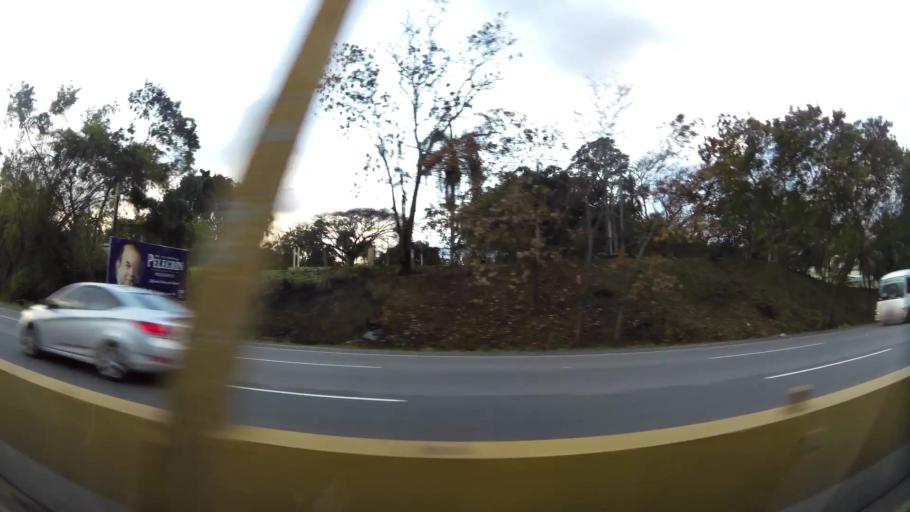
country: DO
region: Santo Domingo
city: Santo Domingo Oeste
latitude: 18.5606
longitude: -70.0614
